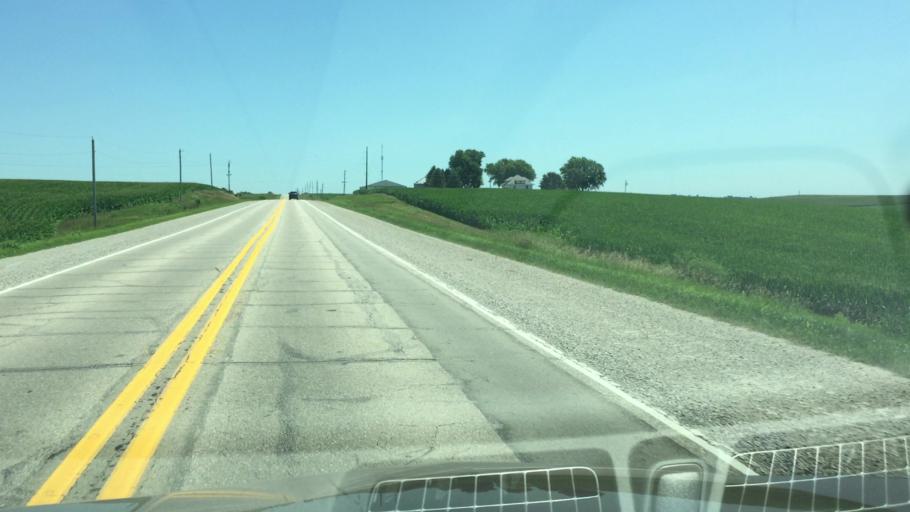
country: US
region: Iowa
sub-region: Cedar County
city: Mechanicsville
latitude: 41.8886
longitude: -91.1949
